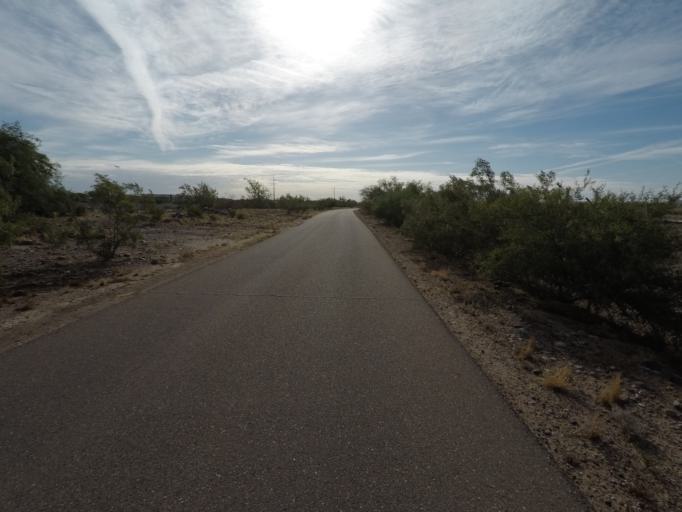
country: US
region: Arizona
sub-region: Maricopa County
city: Phoenix
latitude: 33.4196
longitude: -112.0592
